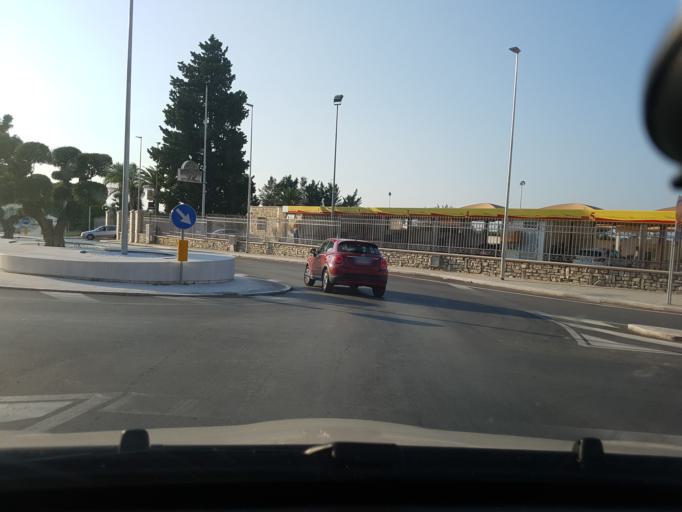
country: IT
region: Apulia
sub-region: Provincia di Foggia
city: Cerignola
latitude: 41.2670
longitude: 15.8857
